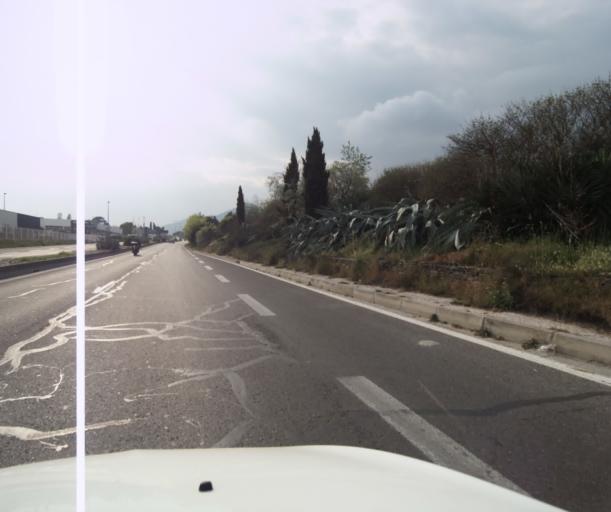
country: FR
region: Provence-Alpes-Cote d'Azur
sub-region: Departement du Var
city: La Garde
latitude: 43.1393
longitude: 6.0140
